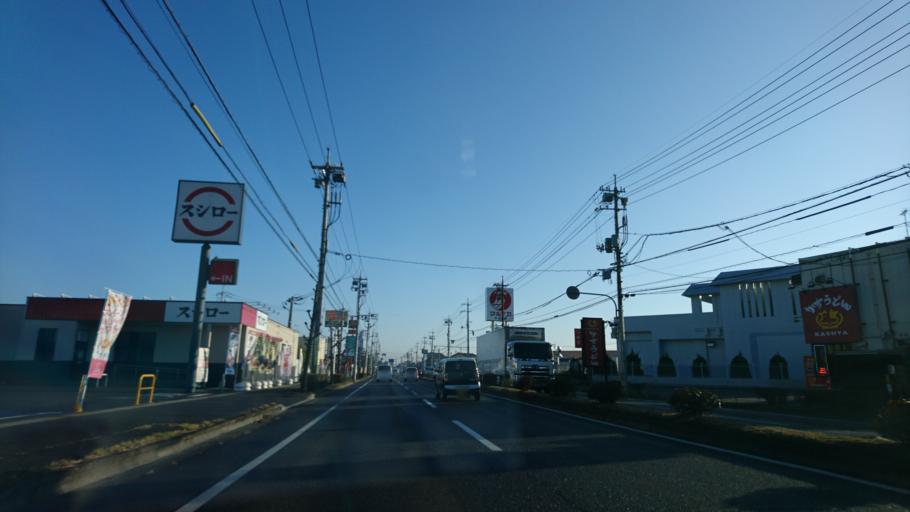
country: JP
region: Okayama
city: Kurashiki
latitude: 34.6114
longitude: 133.7653
